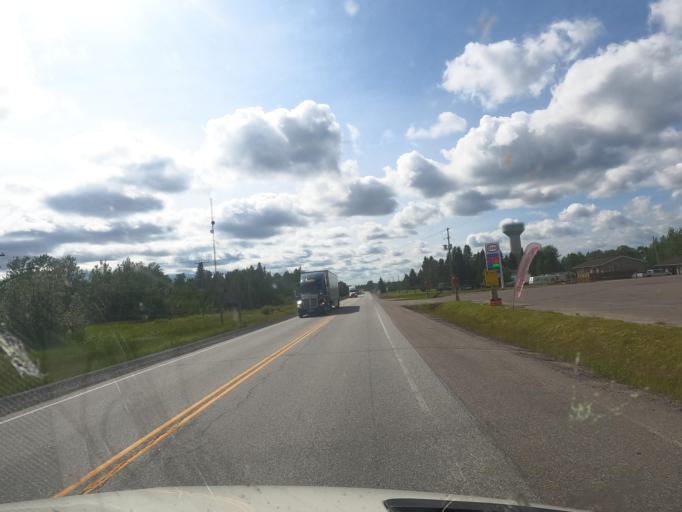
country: CA
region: Ontario
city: Kapuskasing
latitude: 49.2733
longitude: -81.6197
